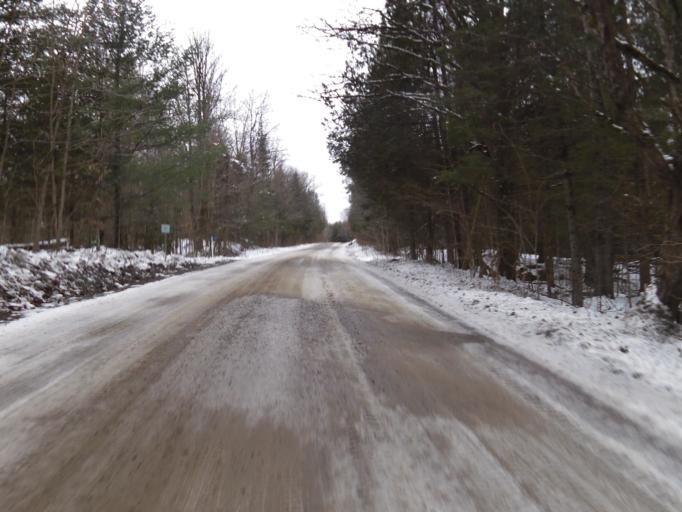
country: CA
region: Ontario
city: Carleton Place
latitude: 45.1450
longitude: -76.2507
